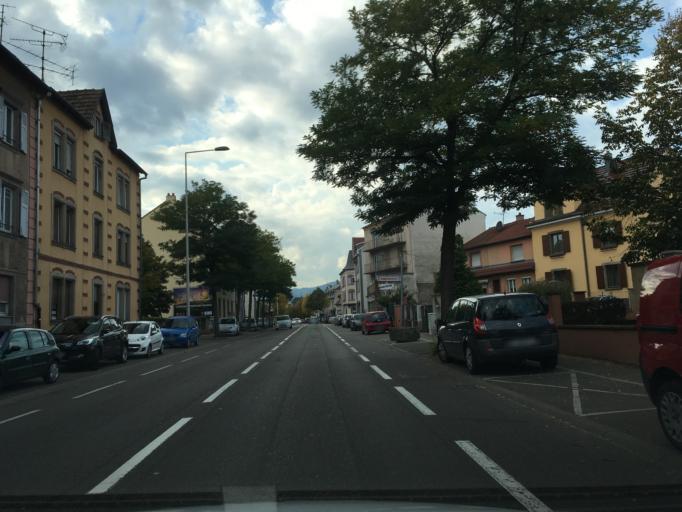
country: FR
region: Alsace
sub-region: Departement du Haut-Rhin
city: Colmar
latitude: 48.0848
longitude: 7.3413
